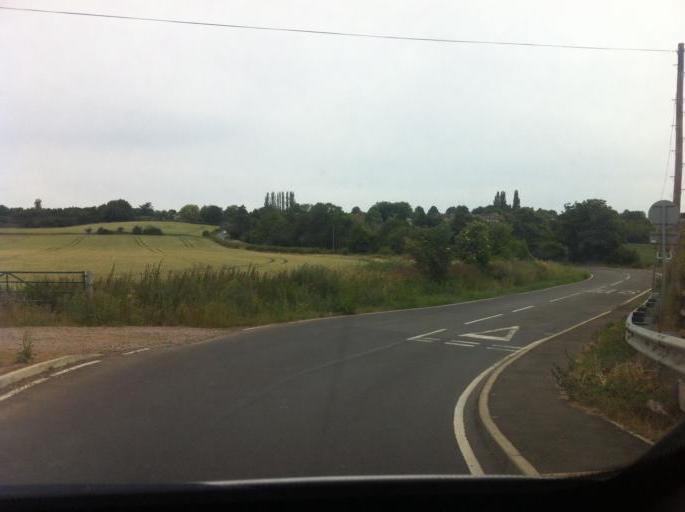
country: GB
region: England
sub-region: Northamptonshire
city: Earls Barton
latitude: 52.2649
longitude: -0.7175
